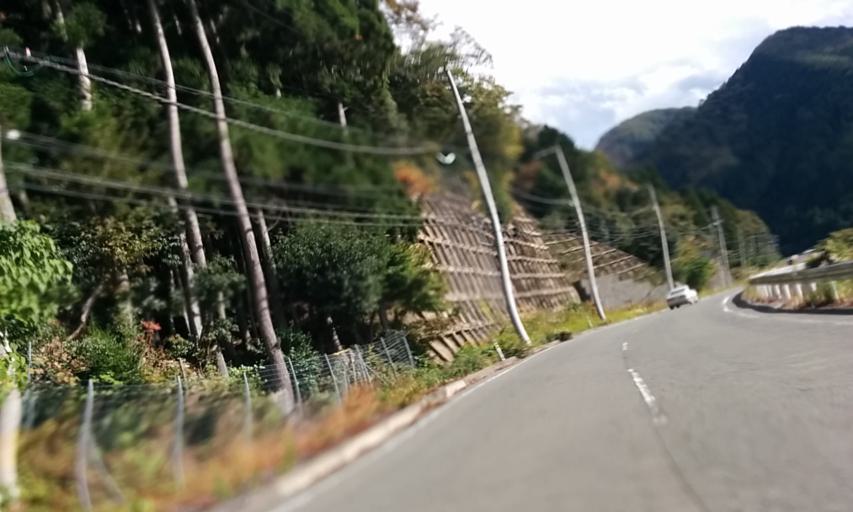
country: JP
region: Fukui
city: Obama
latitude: 35.4025
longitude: 135.6213
